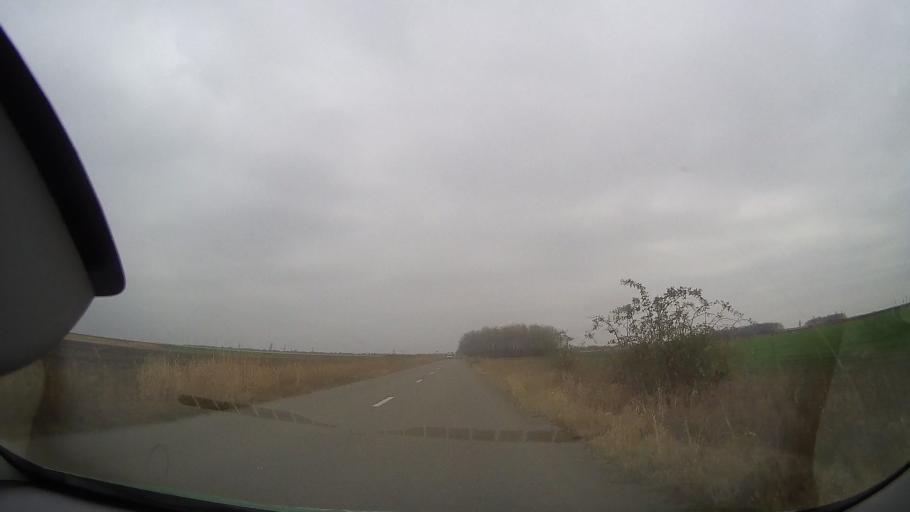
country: RO
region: Buzau
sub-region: Comuna Scutelnici
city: Scutelnici
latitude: 44.8638
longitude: 26.8966
